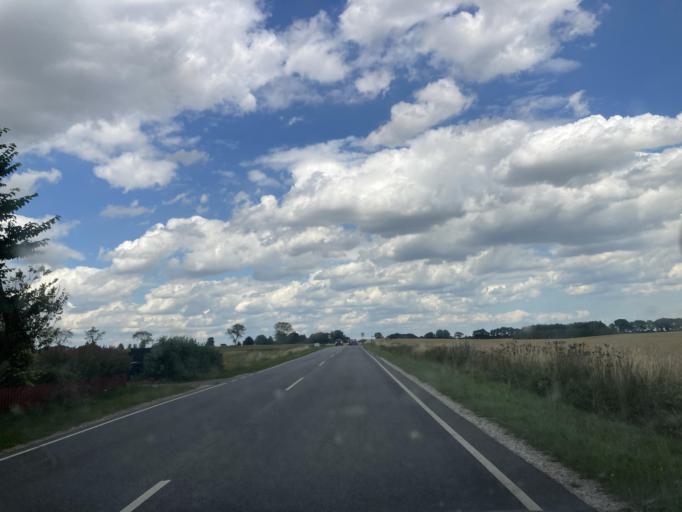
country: DK
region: Zealand
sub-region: Faxe Kommune
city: Haslev
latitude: 55.3356
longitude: 12.0259
